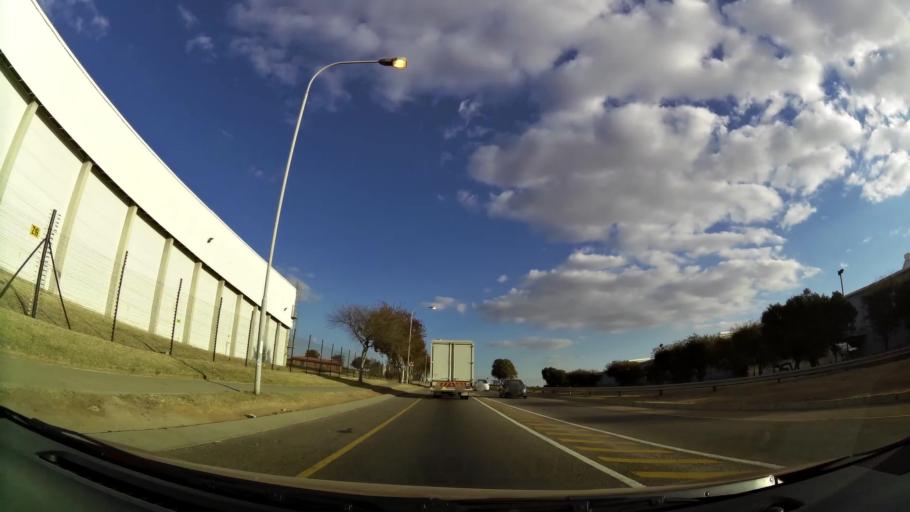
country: ZA
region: Gauteng
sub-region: City of Tshwane Metropolitan Municipality
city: Centurion
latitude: -25.9129
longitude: 28.1644
